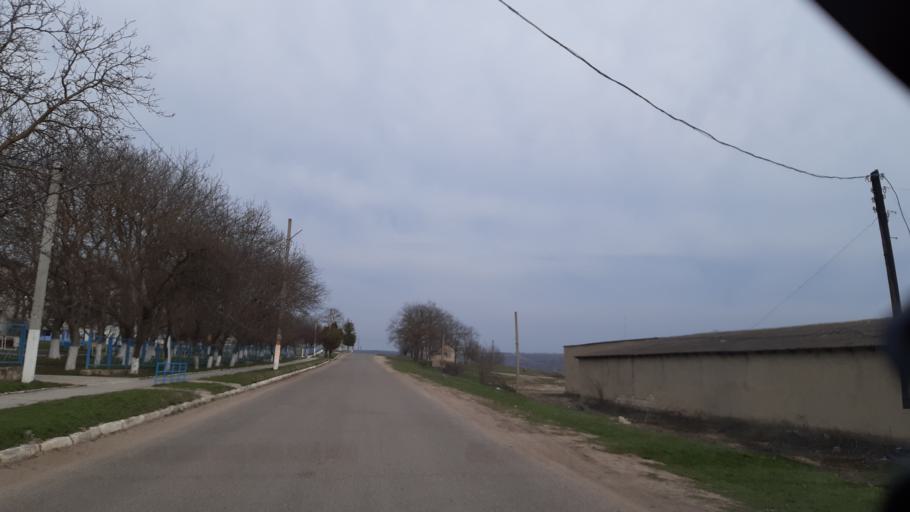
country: MD
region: Soldanesti
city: Soldanesti
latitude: 47.6842
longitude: 28.7685
